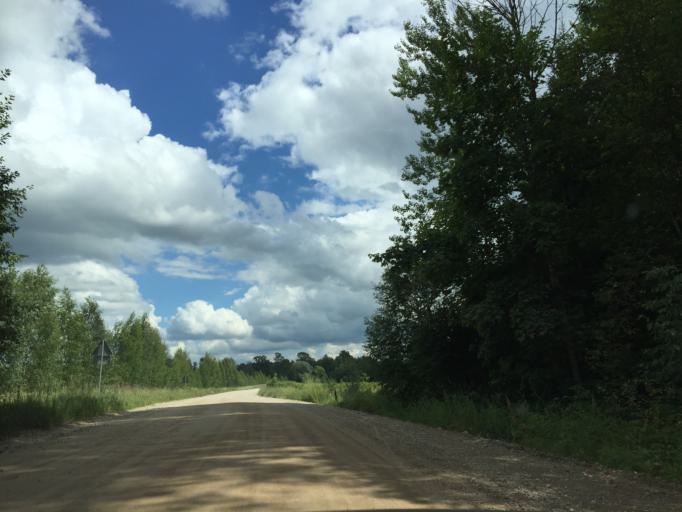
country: LV
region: Ropazu
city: Ropazi
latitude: 56.9090
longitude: 24.7676
